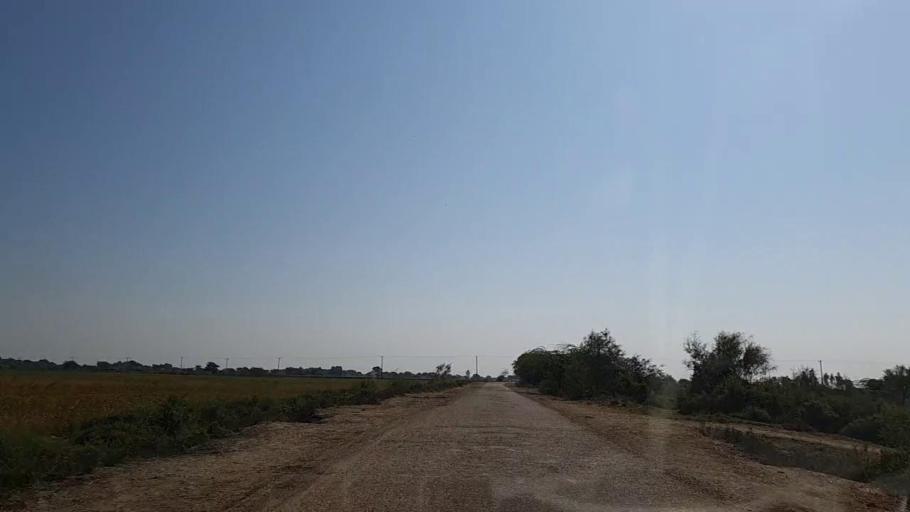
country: PK
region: Sindh
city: Chuhar Jamali
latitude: 24.5227
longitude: 68.0917
